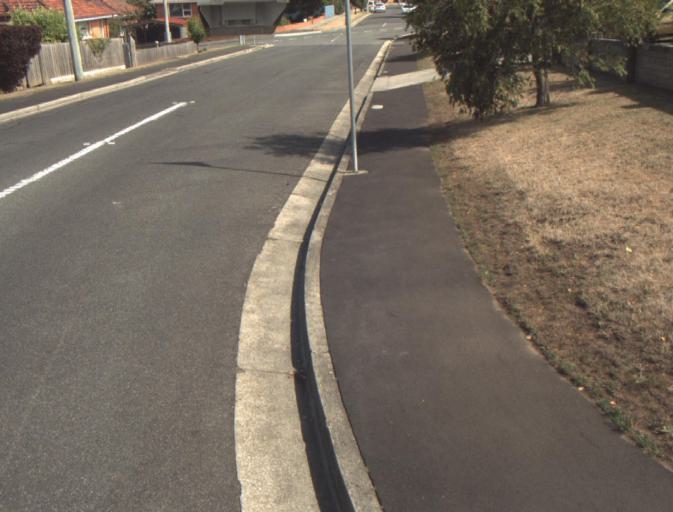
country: AU
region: Tasmania
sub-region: Launceston
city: Mayfield
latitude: -41.3870
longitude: 147.1244
